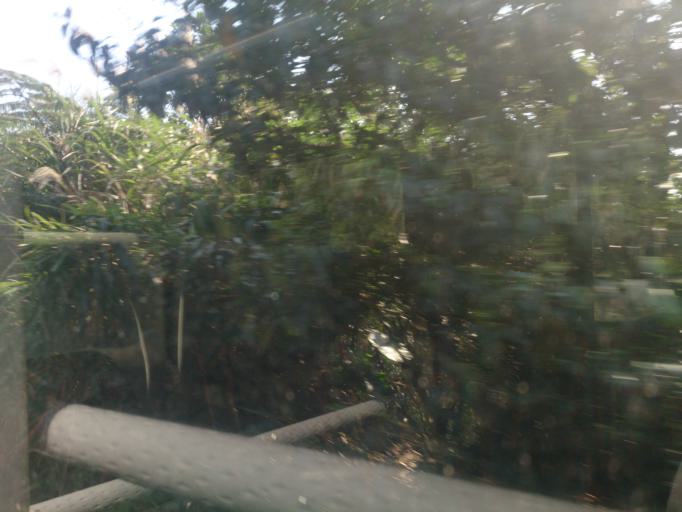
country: TW
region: Taipei
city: Taipei
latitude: 25.1803
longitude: 121.5454
